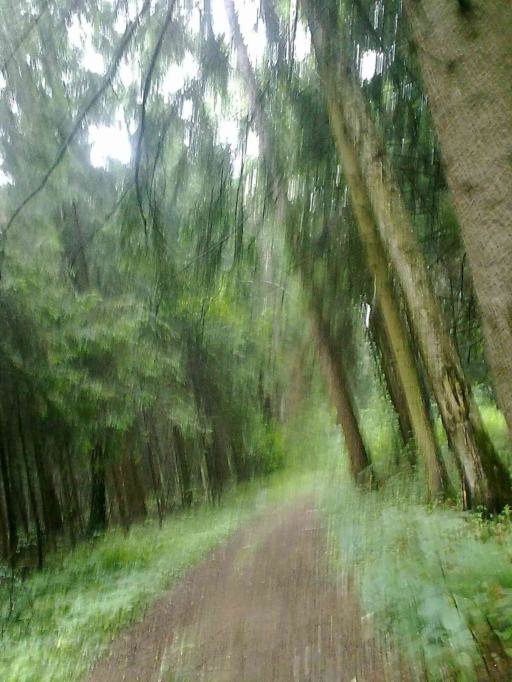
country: RU
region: Moskovskaya
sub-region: Leninskiy Rayon
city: Vnukovo
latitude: 55.6397
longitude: 37.2968
